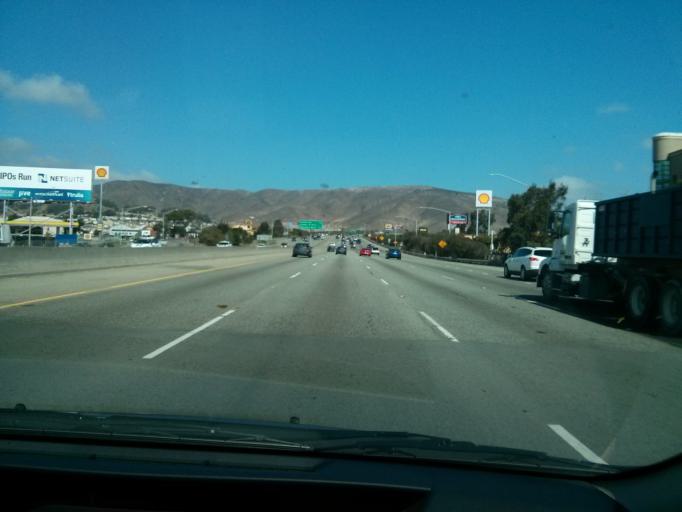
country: US
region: California
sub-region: San Mateo County
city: South San Francisco
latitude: 37.6468
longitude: -122.4063
